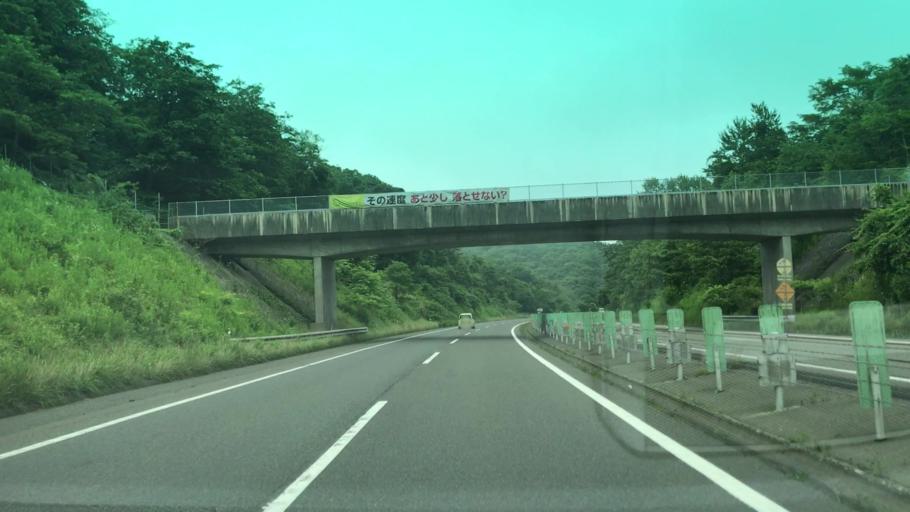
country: JP
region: Hokkaido
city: Shiraoi
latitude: 42.4816
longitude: 141.2219
